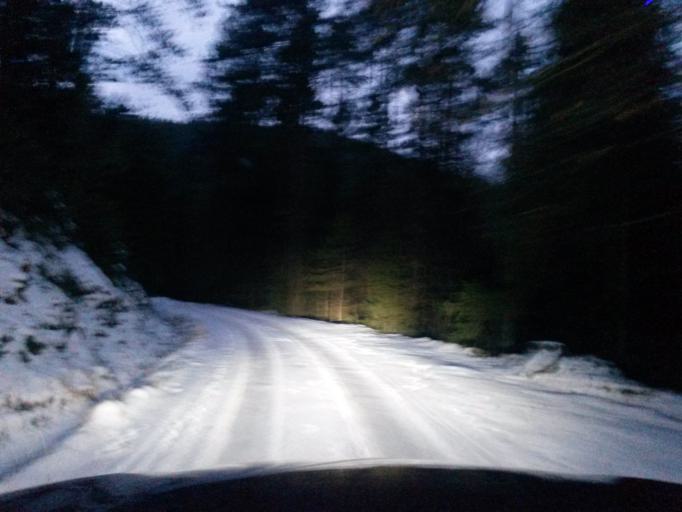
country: SK
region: Kosicky
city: Medzev
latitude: 48.7859
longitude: 20.8040
